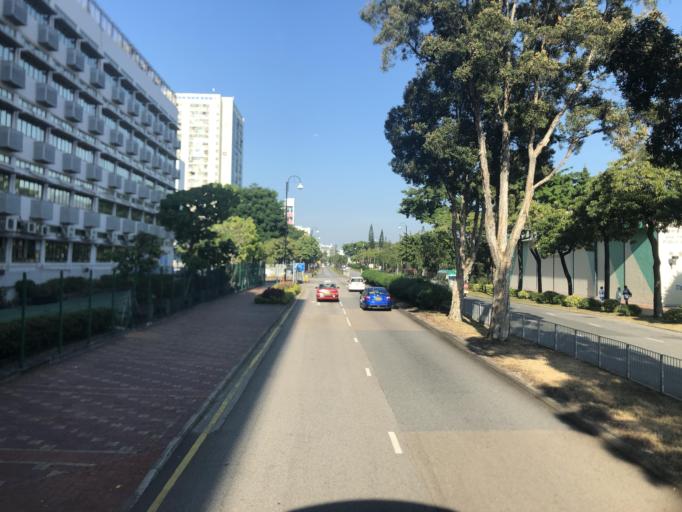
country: HK
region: Sha Tin
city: Sha Tin
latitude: 22.3845
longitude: 114.1934
